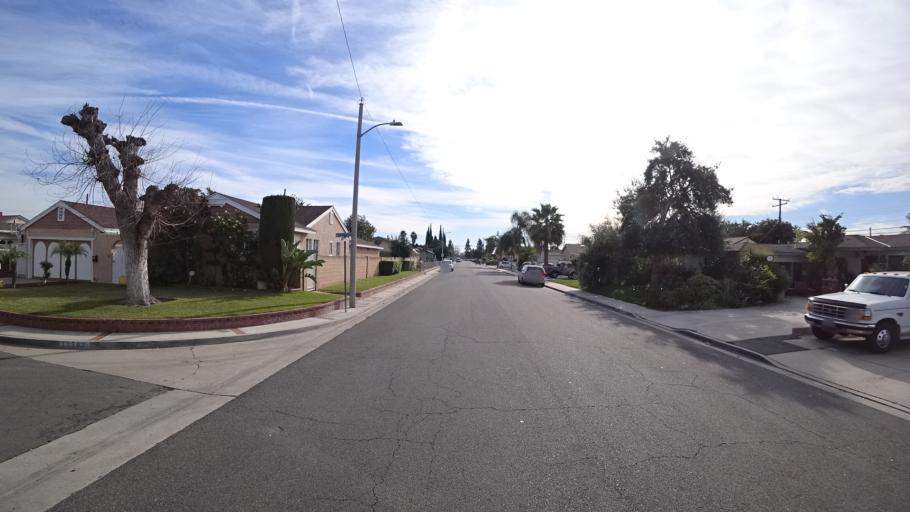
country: US
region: California
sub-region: Orange County
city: Garden Grove
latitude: 33.7704
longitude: -117.9069
